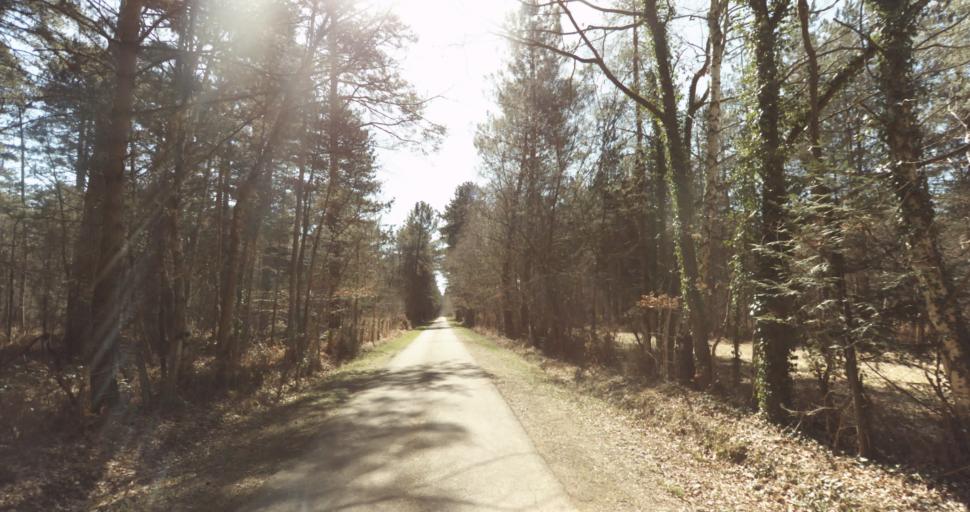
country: FR
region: Lower Normandy
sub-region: Departement du Calvados
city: Saint-Pierre-sur-Dives
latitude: 49.0070
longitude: 0.0574
